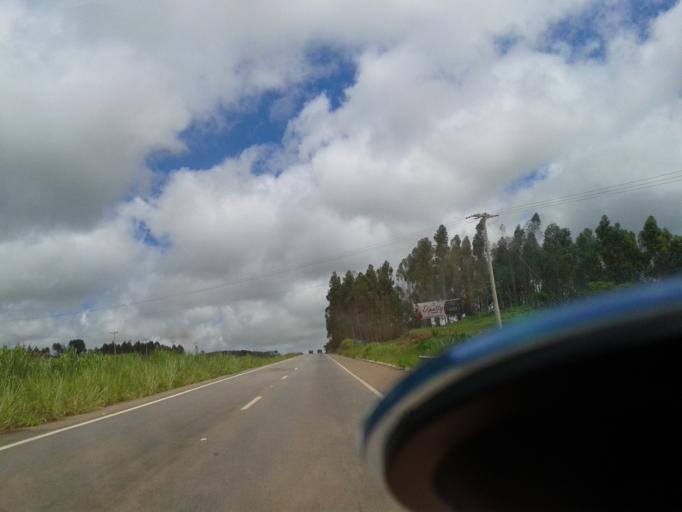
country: BR
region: Goias
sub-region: Inhumas
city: Inhumas
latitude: -16.1739
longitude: -49.6191
